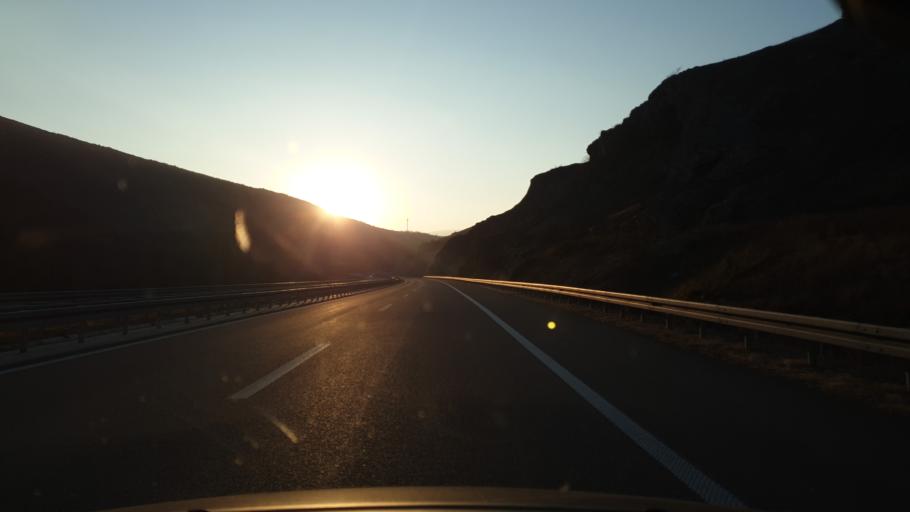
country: RS
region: Central Serbia
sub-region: Pirotski Okrug
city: Bela Palanka
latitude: 43.2227
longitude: 22.4248
